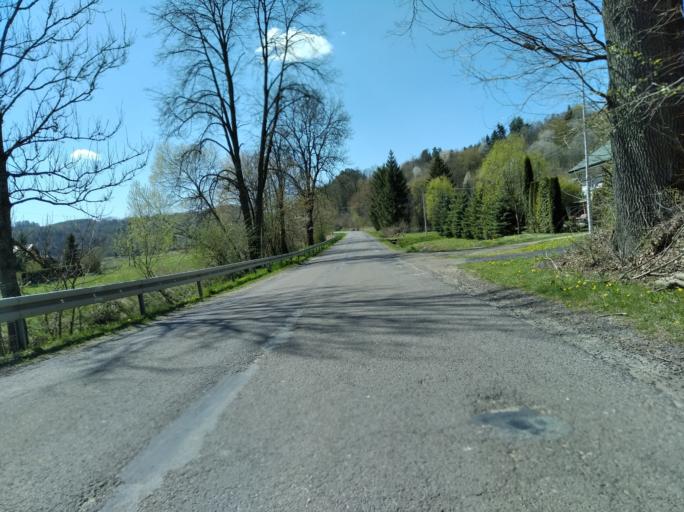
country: PL
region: Subcarpathian Voivodeship
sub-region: Powiat brzozowski
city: Dydnia
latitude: 49.7044
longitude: 22.1961
